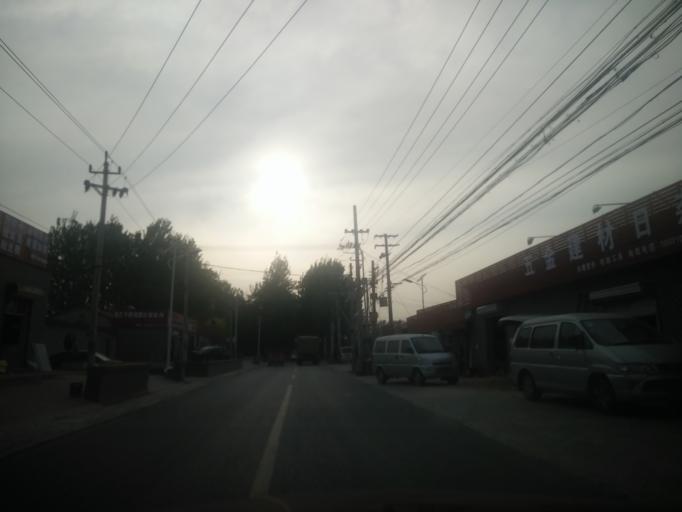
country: CN
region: Beijing
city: Qingyundian
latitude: 39.6790
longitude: 116.4748
